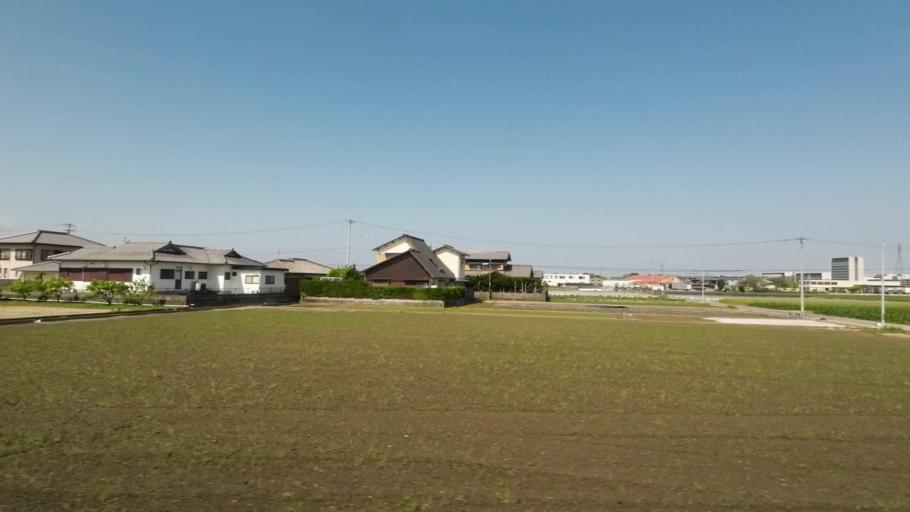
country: JP
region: Kagawa
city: Kan'onjicho
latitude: 34.1117
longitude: 133.6490
